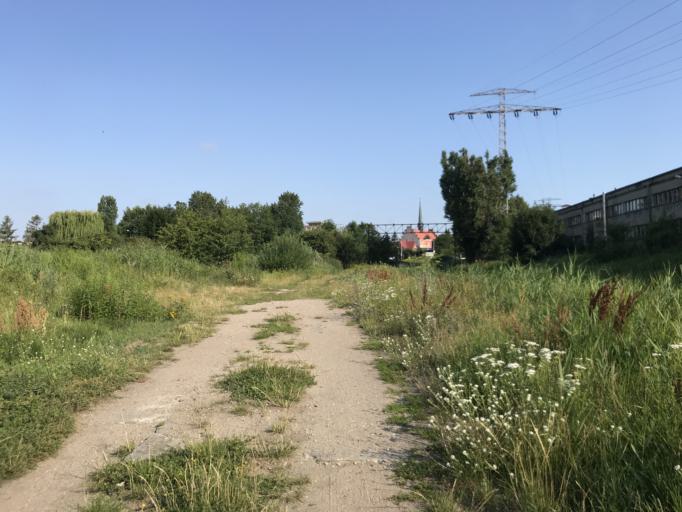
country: PL
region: Pomeranian Voivodeship
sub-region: Gdansk
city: Gdansk
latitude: 54.3476
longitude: 18.6777
